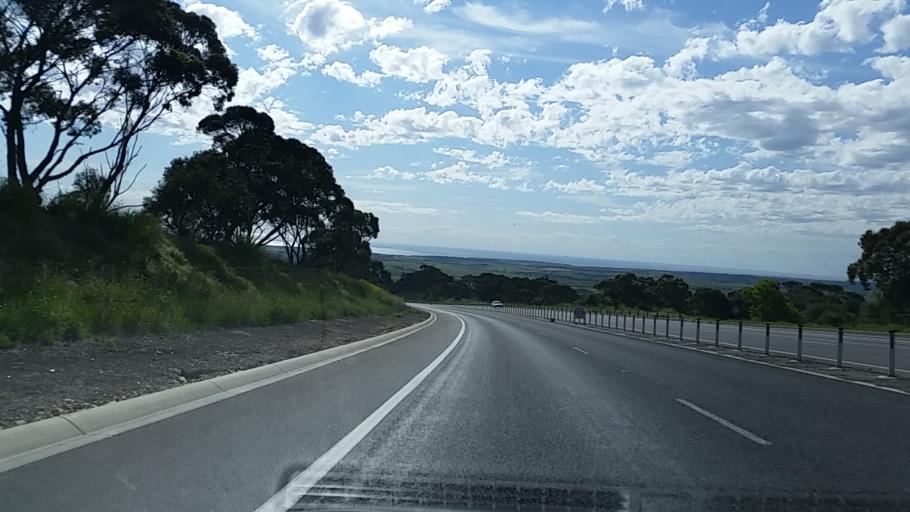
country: AU
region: South Australia
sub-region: Onkaparinga
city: McLaren Vale
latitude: -35.2831
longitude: 138.5660
